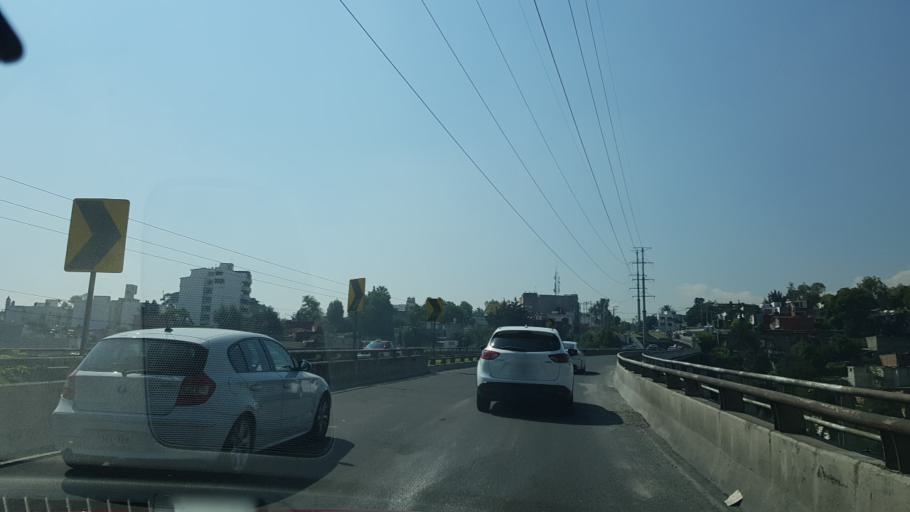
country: MX
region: Mexico City
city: Alvaro Obregon
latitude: 19.3630
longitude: -99.2057
